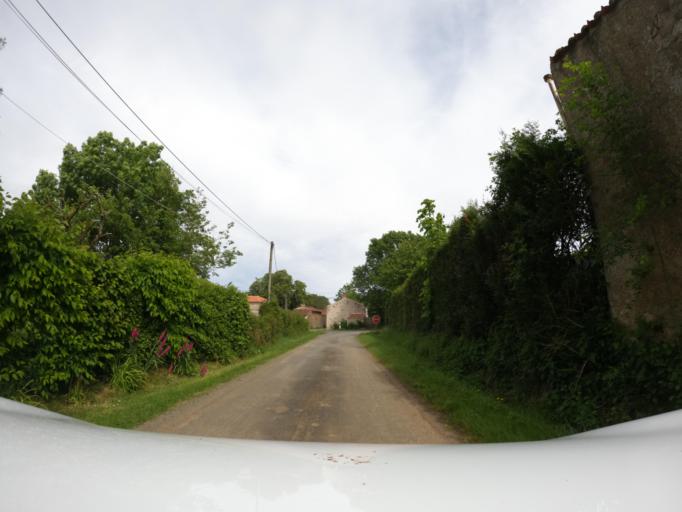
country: FR
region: Pays de la Loire
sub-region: Departement de la Vendee
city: Saint-Hilaire-des-Loges
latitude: 46.4993
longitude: -0.6525
